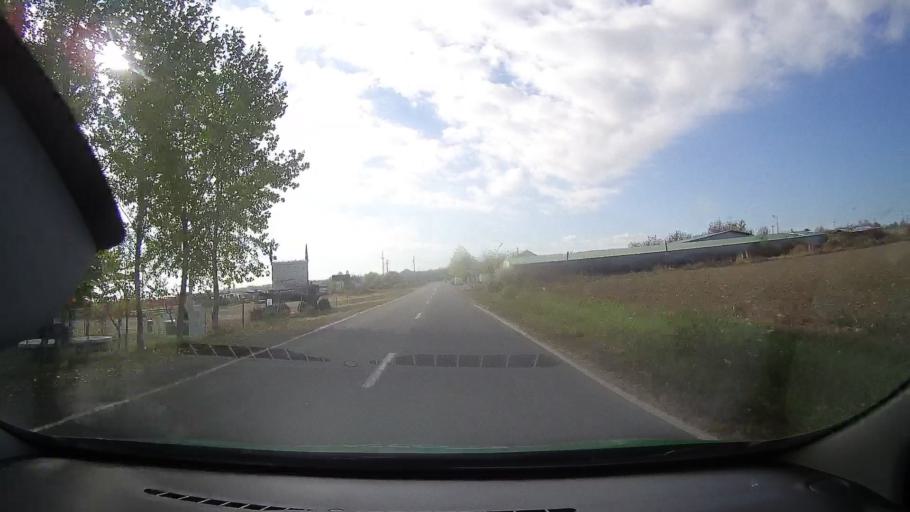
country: RO
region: Tulcea
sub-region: Comuna Sarichioi
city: Sarichioi
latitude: 44.9580
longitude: 28.8574
